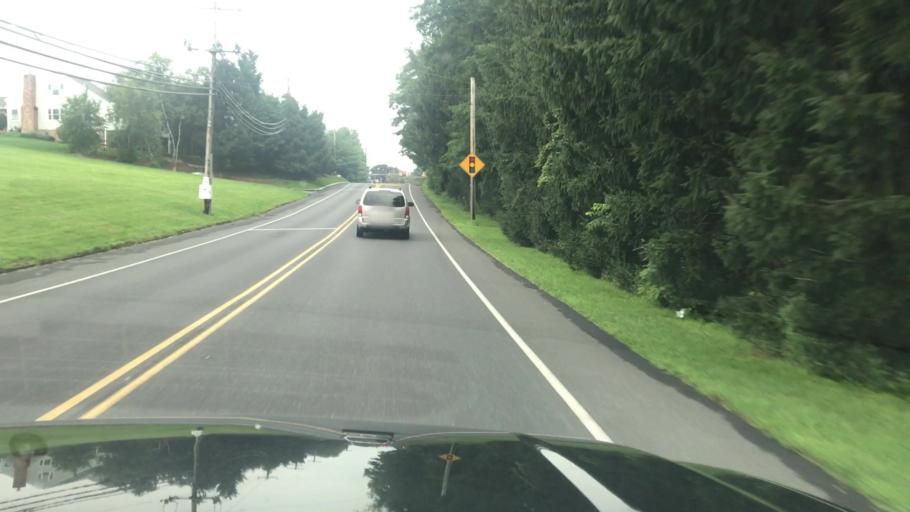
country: US
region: Pennsylvania
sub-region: Cumberland County
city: Enola
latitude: 40.2697
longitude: -76.9673
